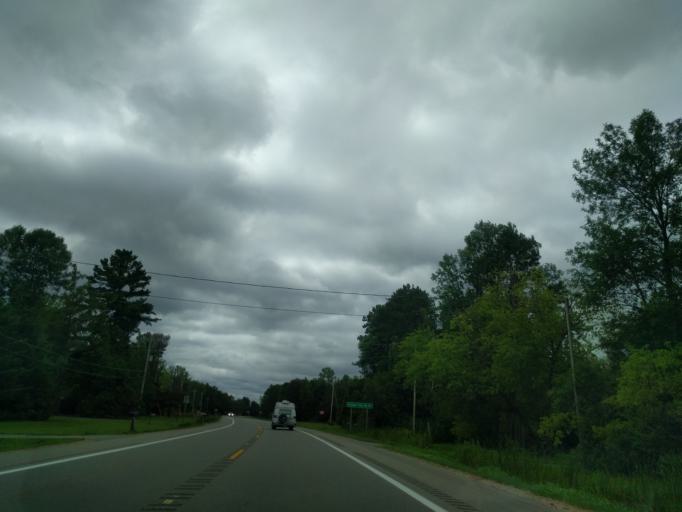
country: US
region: Michigan
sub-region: Menominee County
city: Menominee
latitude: 45.1794
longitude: -87.5691
